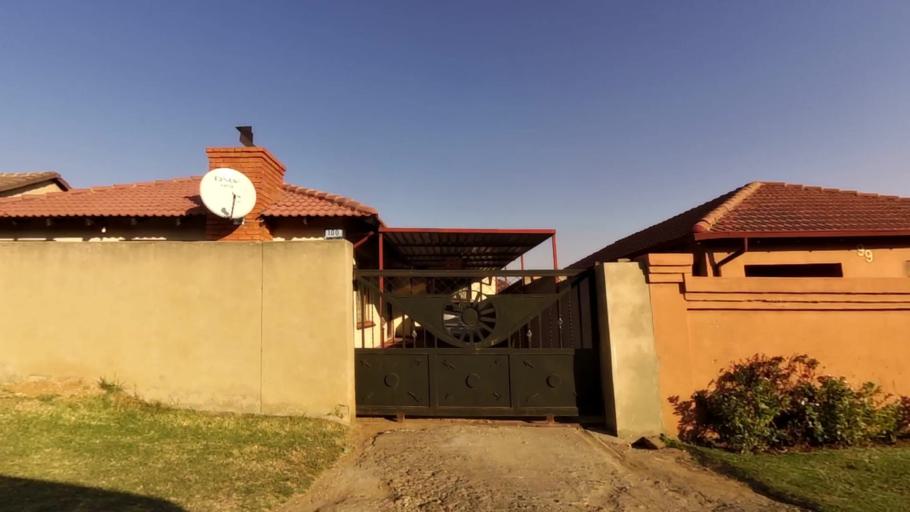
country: ZA
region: Gauteng
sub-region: City of Johannesburg Metropolitan Municipality
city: Johannesburg
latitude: -26.2792
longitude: 27.9667
